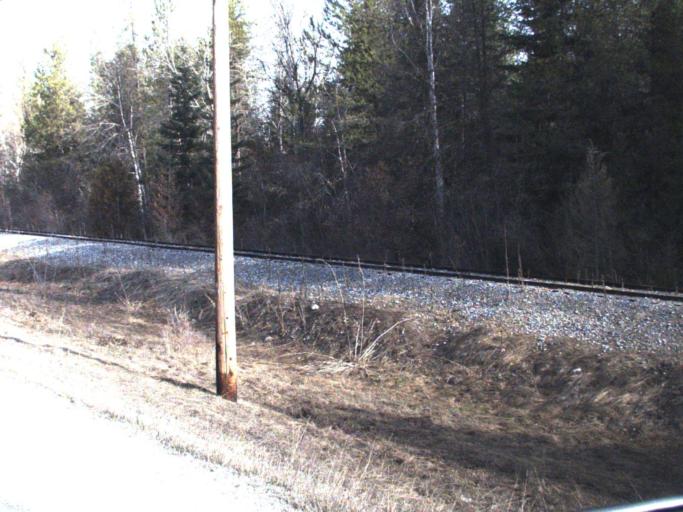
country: US
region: Washington
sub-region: Stevens County
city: Chewelah
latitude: 48.6446
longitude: -117.3763
